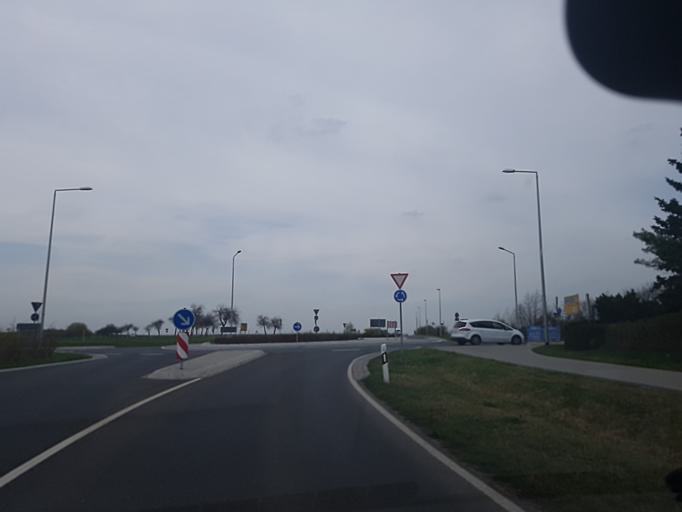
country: DE
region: Saxony
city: Oschatz
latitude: 51.2950
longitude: 13.0918
